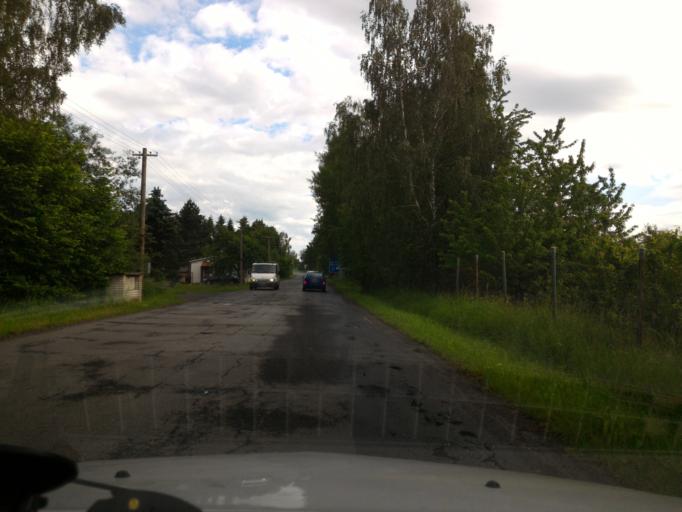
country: CZ
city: Jablonne v Podjestedi
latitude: 50.7718
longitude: 14.7682
